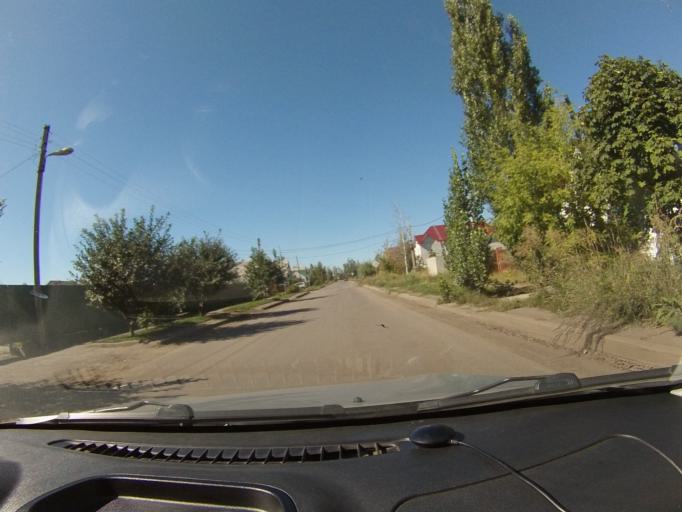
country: RU
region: Tambov
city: Komsomolets
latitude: 52.7664
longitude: 41.3671
